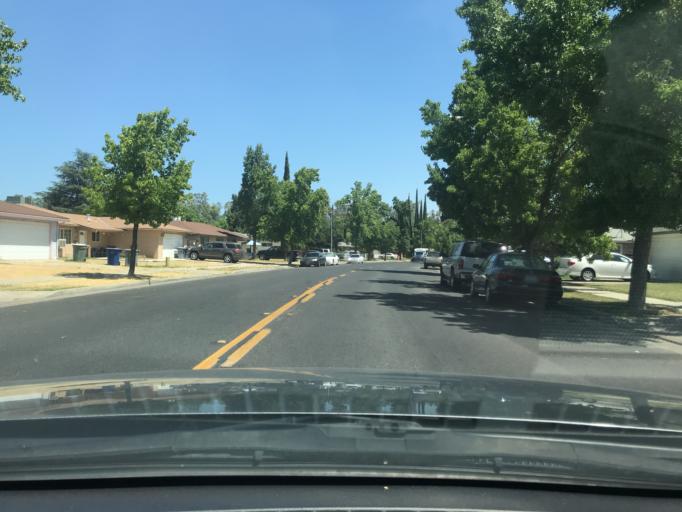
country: US
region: California
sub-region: Merced County
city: Merced
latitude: 37.3207
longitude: -120.4997
